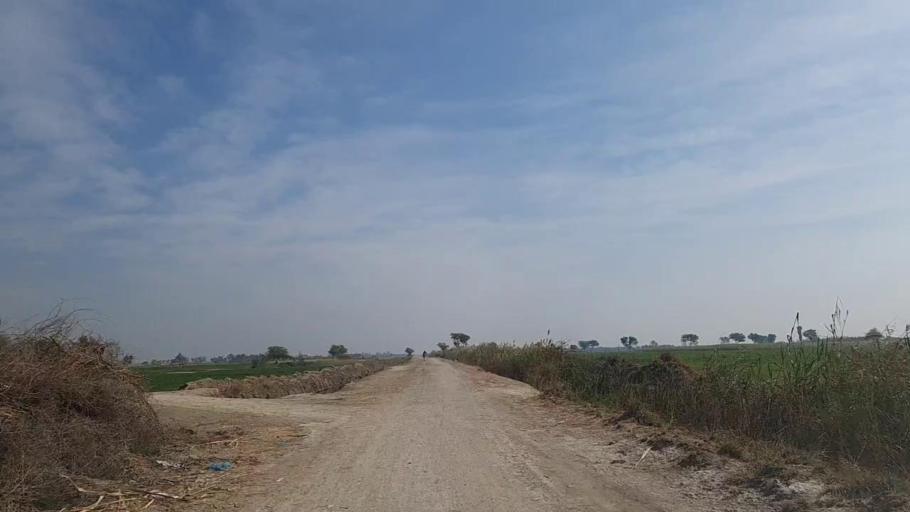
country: PK
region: Sindh
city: Nawabshah
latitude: 26.3320
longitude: 68.4477
